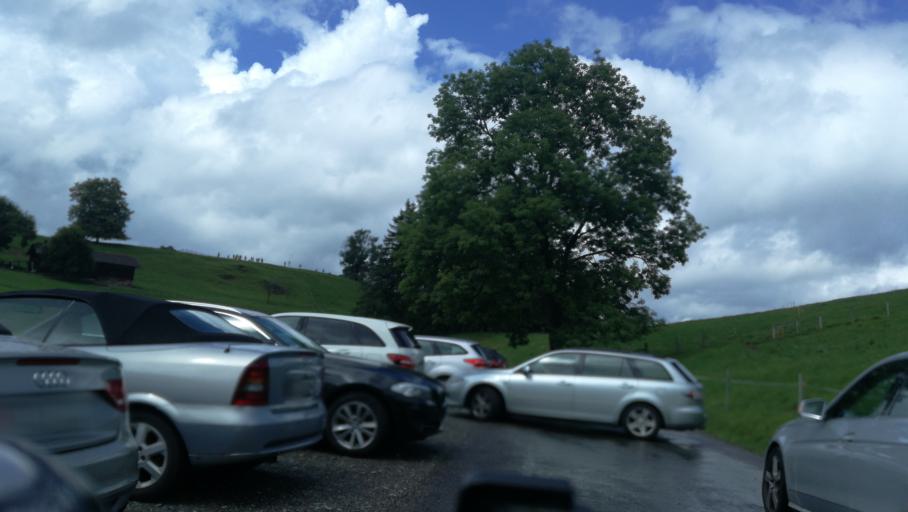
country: CH
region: Zug
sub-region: Zug
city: Zug
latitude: 47.1464
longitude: 8.5383
